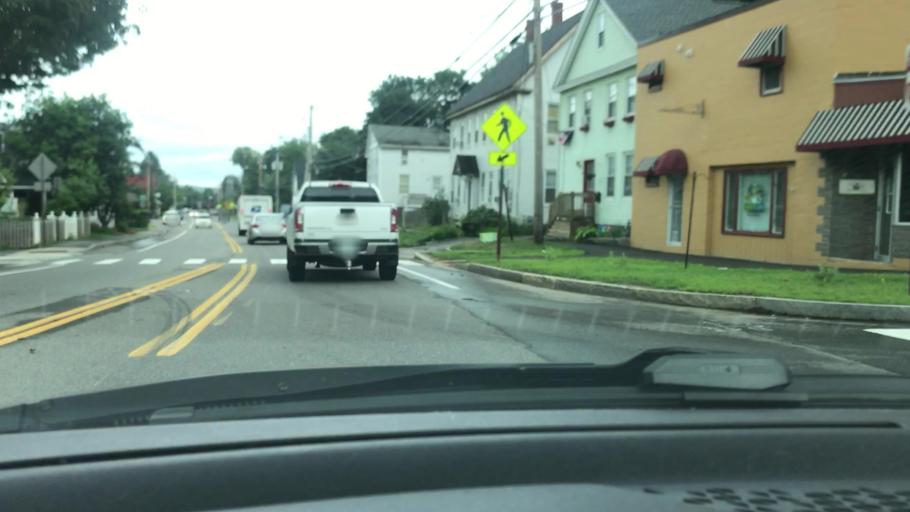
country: US
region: New Hampshire
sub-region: Merrimack County
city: Concord
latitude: 43.2195
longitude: -71.5504
